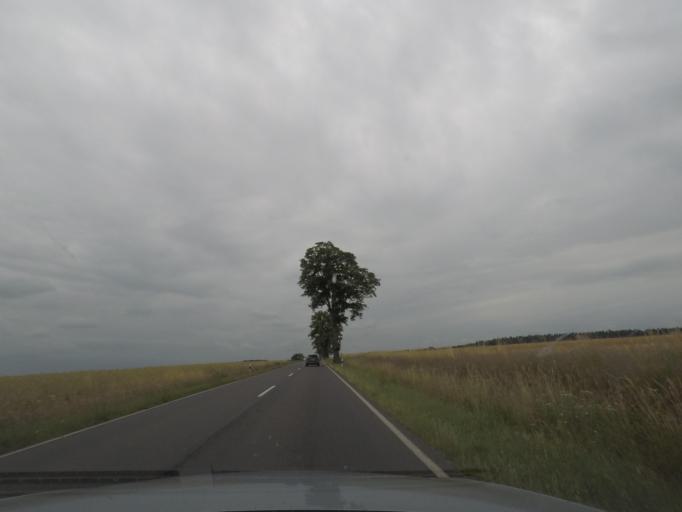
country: DE
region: Saxony-Anhalt
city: Haldensleben I
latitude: 52.2673
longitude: 11.3733
